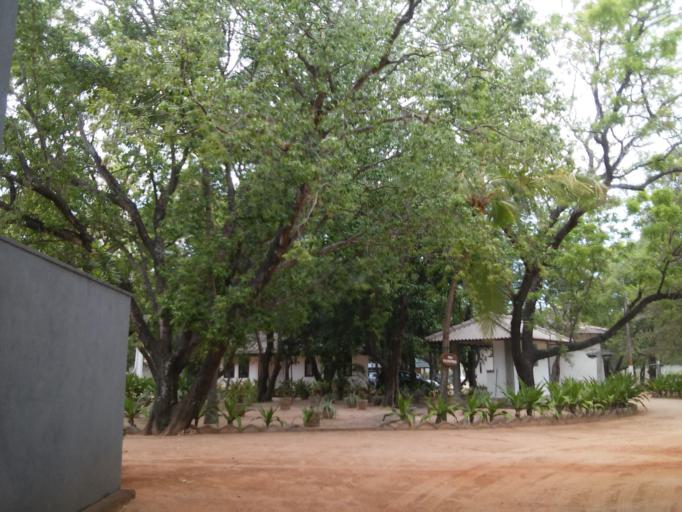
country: LK
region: Eastern Province
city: Trincomalee
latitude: 8.7061
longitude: 81.1883
